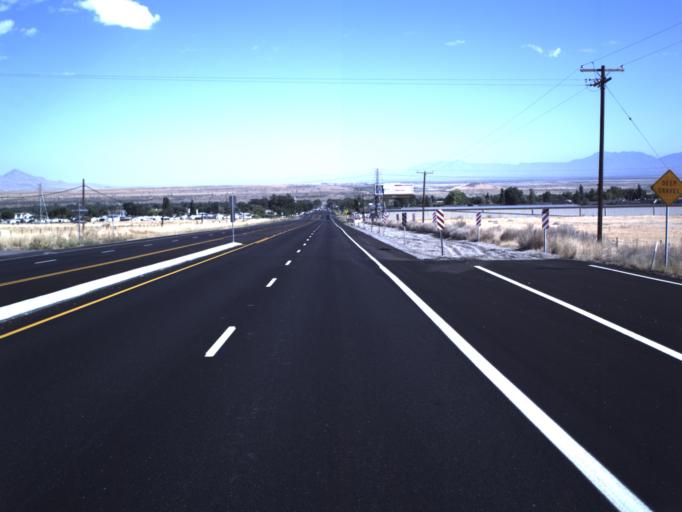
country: US
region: Utah
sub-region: Salt Lake County
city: Magna
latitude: 40.6835
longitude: -112.0918
